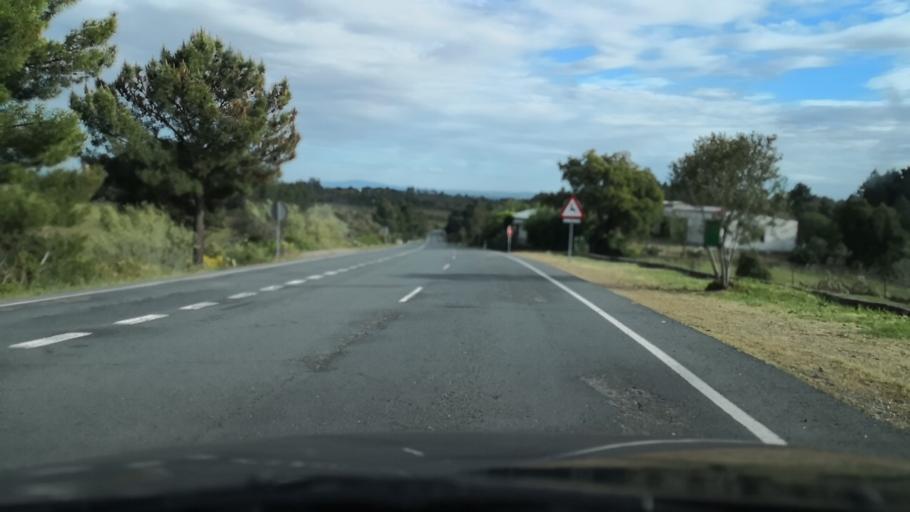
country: ES
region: Extremadura
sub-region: Provincia de Caceres
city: Perales del Puerto
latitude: 40.1520
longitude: -6.6789
